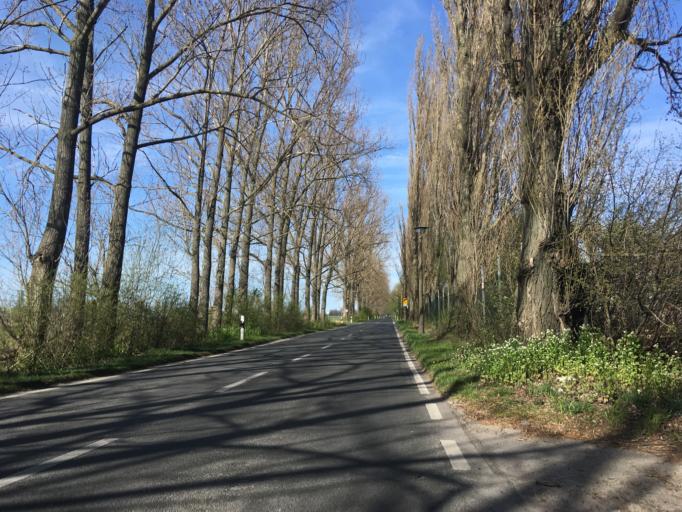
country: DE
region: Berlin
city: Wartenberg
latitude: 52.5830
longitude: 13.5221
